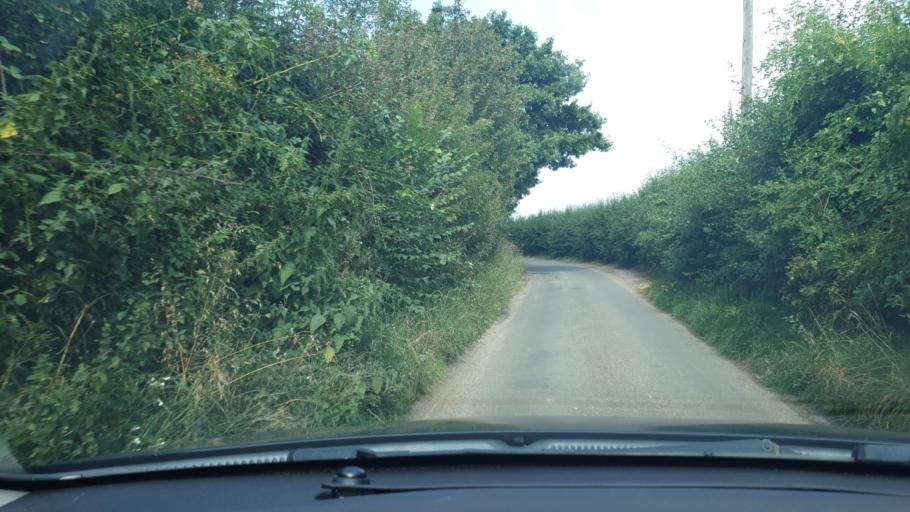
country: GB
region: England
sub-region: Suffolk
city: East Bergholt
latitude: 51.9208
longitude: 0.9997
